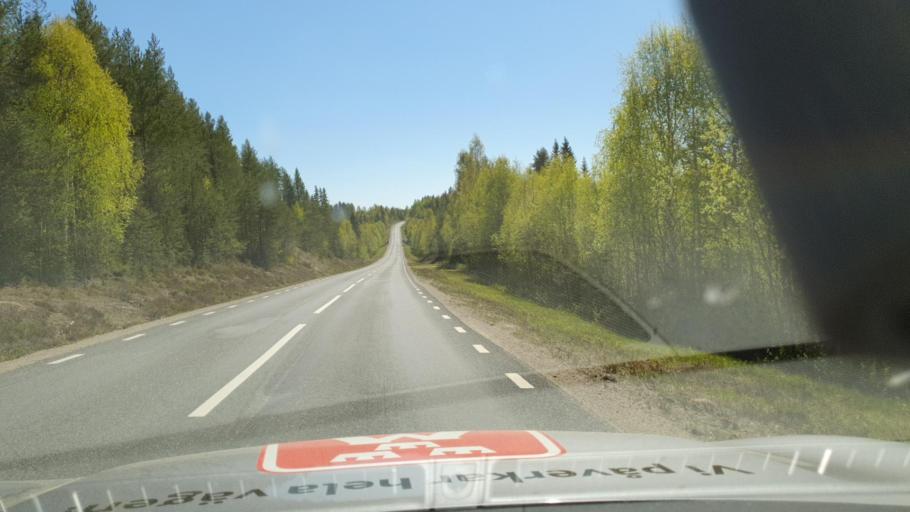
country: SE
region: Vaesternorrland
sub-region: OErnskoeldsviks Kommun
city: Bredbyn
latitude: 63.7752
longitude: 18.4931
